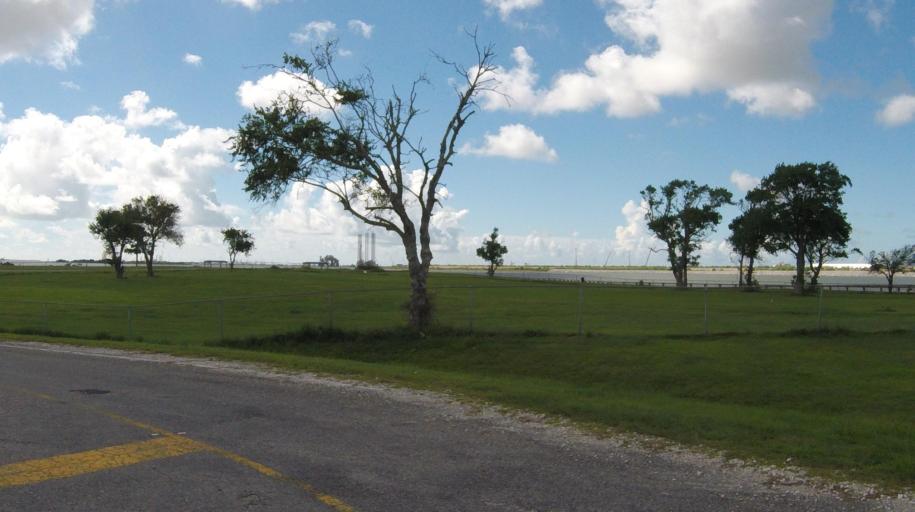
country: US
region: Texas
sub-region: Jefferson County
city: Port Arthur
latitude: 29.7635
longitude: -93.9015
